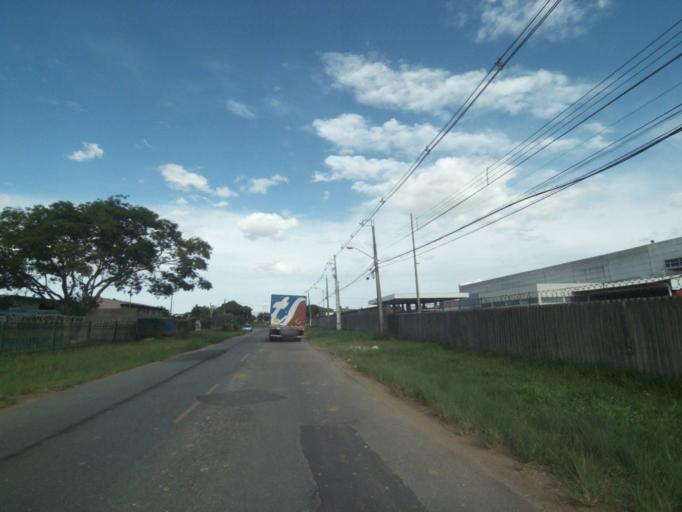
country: BR
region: Parana
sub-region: Curitiba
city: Curitiba
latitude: -25.5007
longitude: -49.3309
